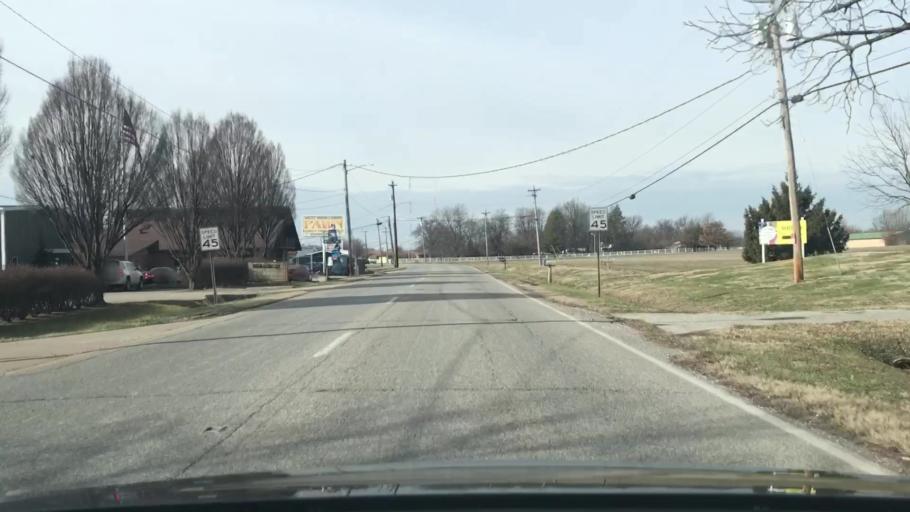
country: US
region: Kentucky
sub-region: Daviess County
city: Owensboro
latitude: 37.7739
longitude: -87.1453
